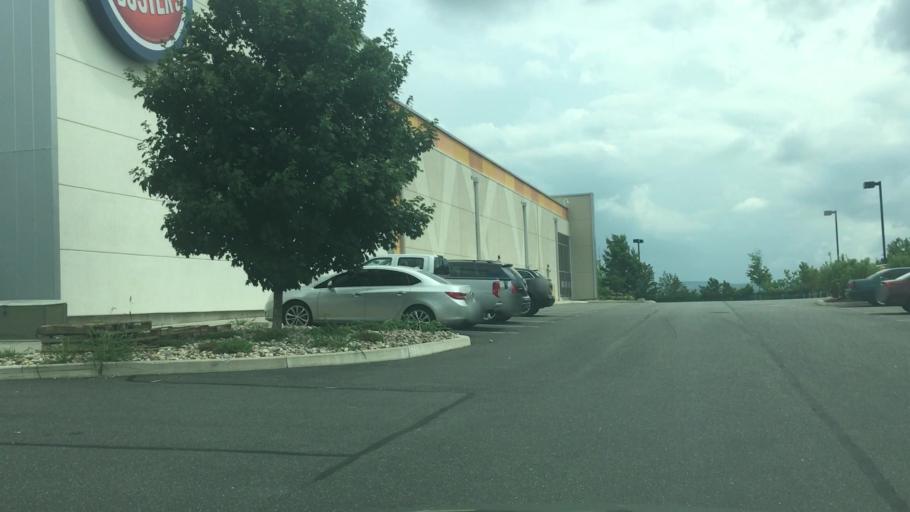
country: US
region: Connecticut
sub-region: Hartford County
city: Manchester
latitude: 41.8074
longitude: -72.5505
